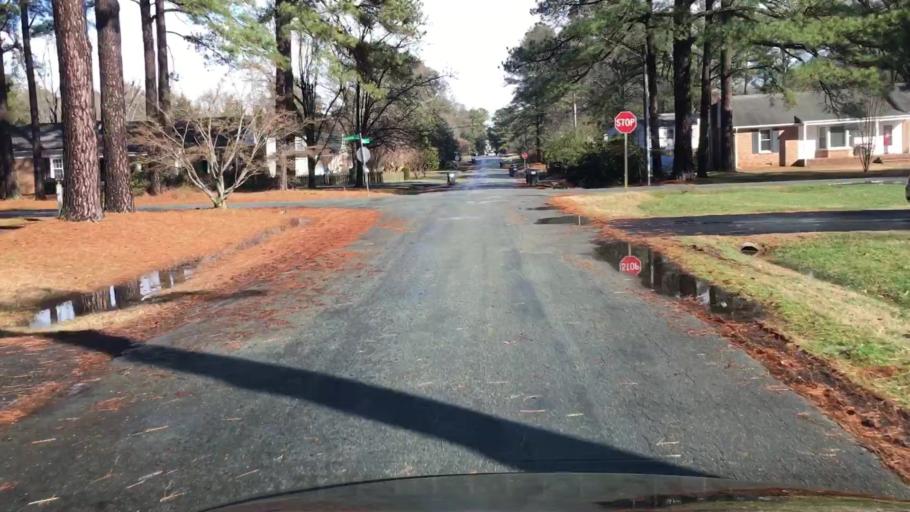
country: US
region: Virginia
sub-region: Chesterfield County
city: Bon Air
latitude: 37.5280
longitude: -77.5933
